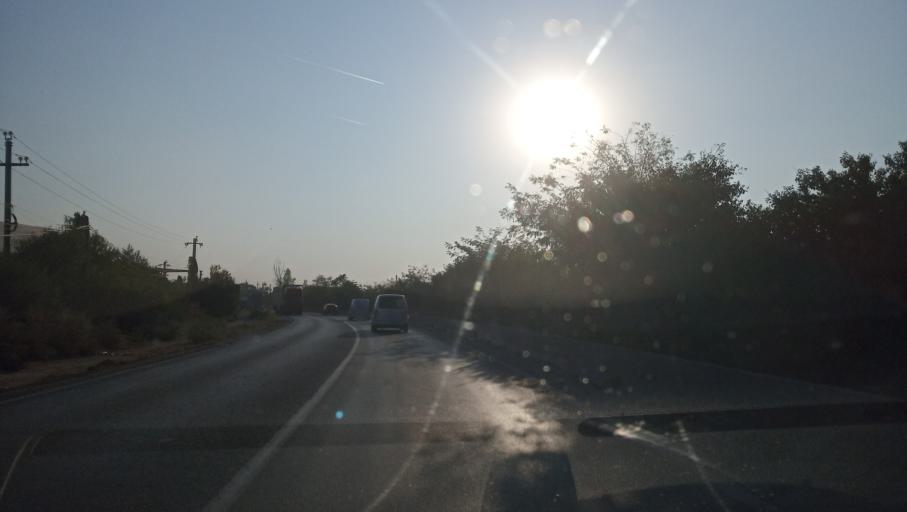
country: RO
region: Ilfov
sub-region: Comuna Glina
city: Catelu
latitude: 44.3788
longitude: 26.2188
